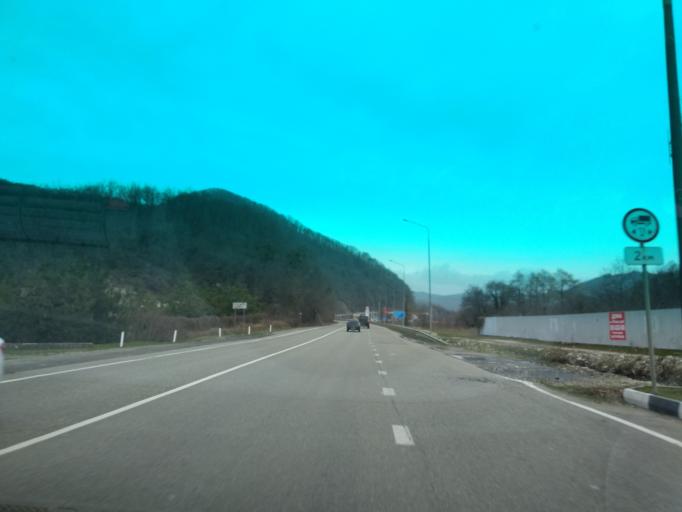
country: RU
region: Krasnodarskiy
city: Ol'ginka
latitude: 44.2144
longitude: 38.8949
